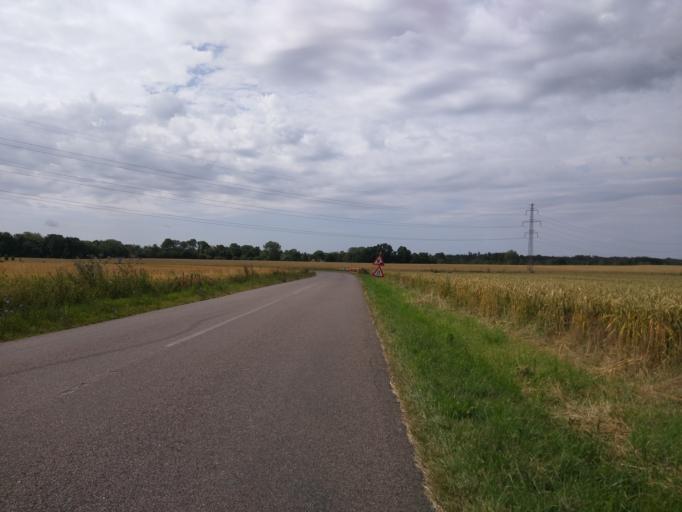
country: DK
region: Zealand
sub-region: Kalundborg Kommune
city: Svebolle
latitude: 55.6910
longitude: 11.3056
